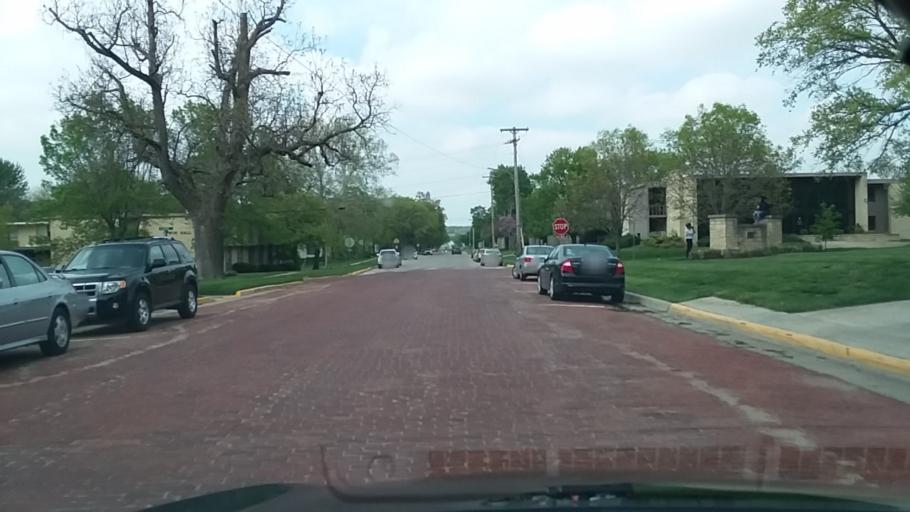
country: US
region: Kansas
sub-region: Douglas County
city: Baldwin City
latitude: 38.7786
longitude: -95.1889
